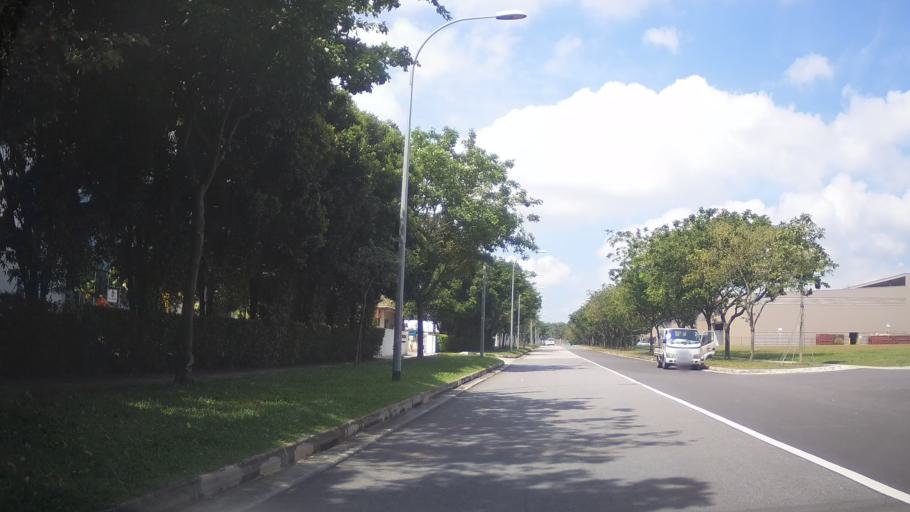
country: SG
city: Singapore
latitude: 1.3237
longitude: 103.7147
